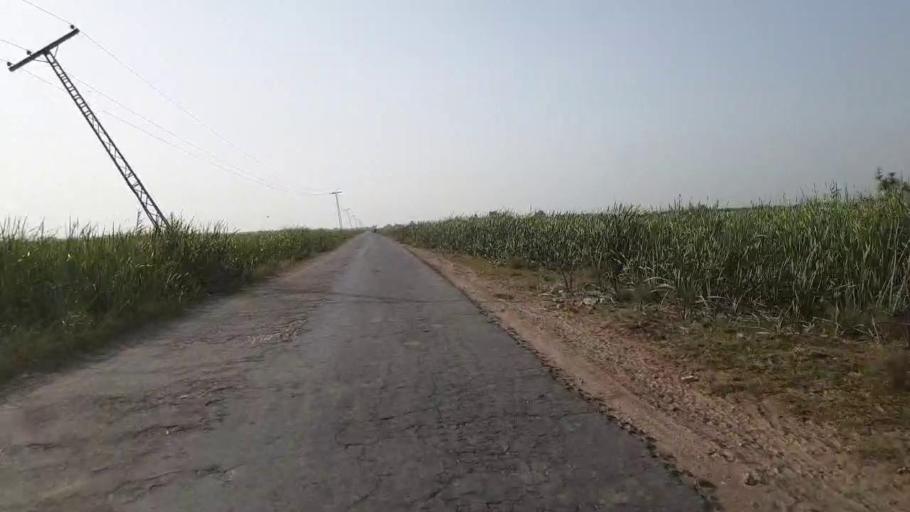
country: PK
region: Sindh
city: Jam Sahib
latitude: 26.4090
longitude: 68.8761
